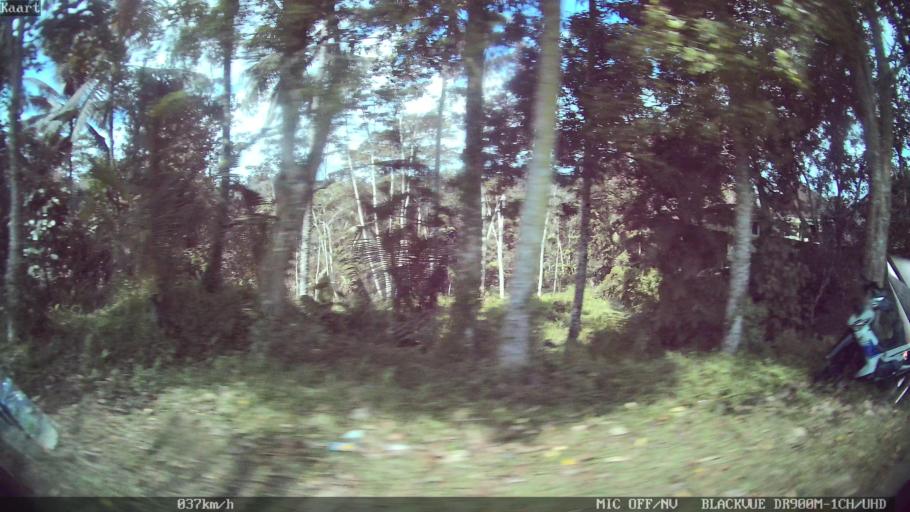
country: ID
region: Bali
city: Banjar Abuan
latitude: -8.4641
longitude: 115.3255
